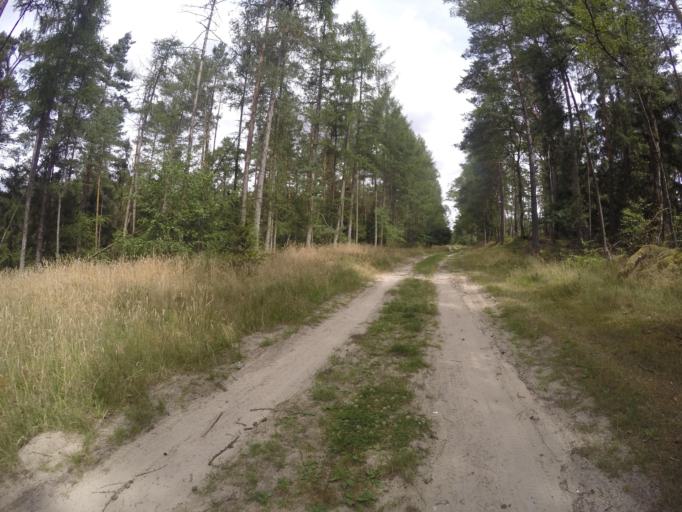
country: DE
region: Lower Saxony
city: Thomasburg
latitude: 53.2488
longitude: 10.6795
